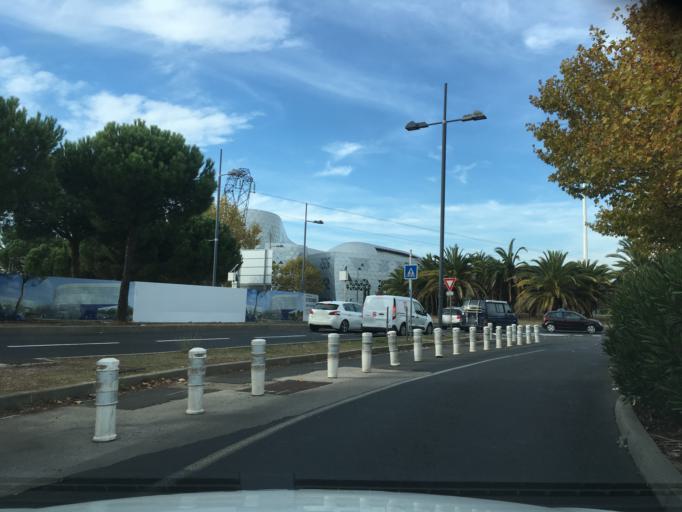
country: FR
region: Languedoc-Roussillon
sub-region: Departement de l'Herault
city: Castelnau-le-Lez
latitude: 43.6037
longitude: 3.9135
